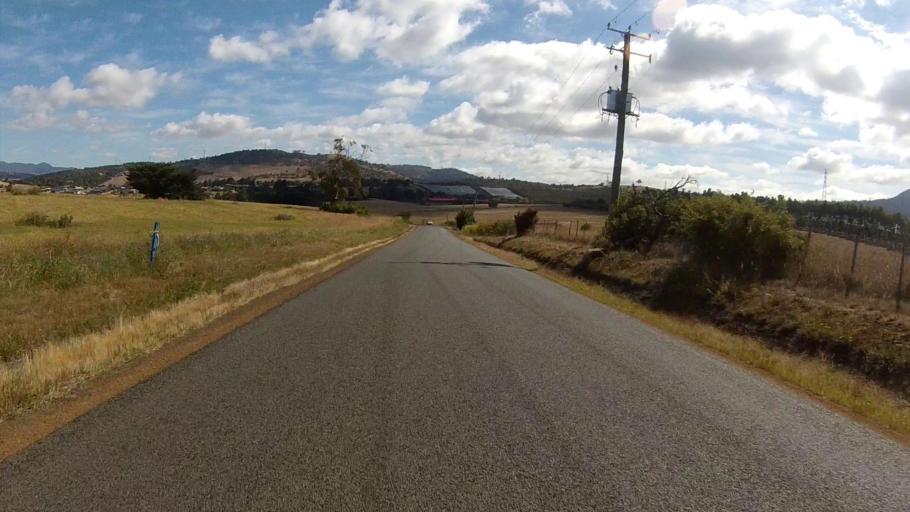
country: AU
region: Tasmania
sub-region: Brighton
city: Old Beach
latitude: -42.7608
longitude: 147.2793
